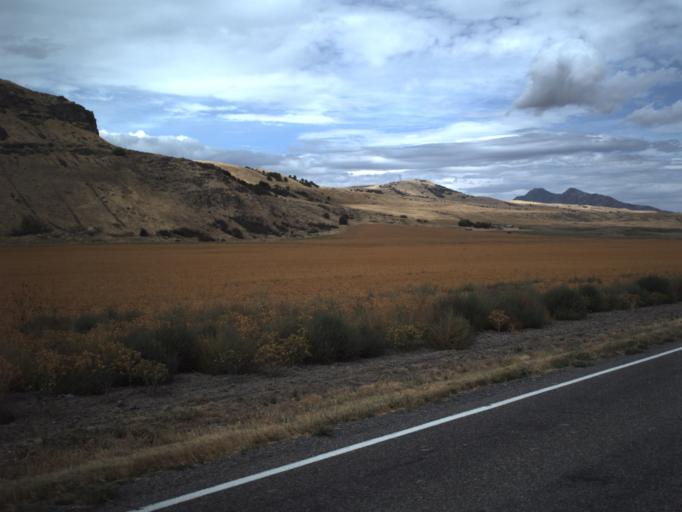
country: US
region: Utah
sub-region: Cache County
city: Benson
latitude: 41.7938
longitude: -111.9896
